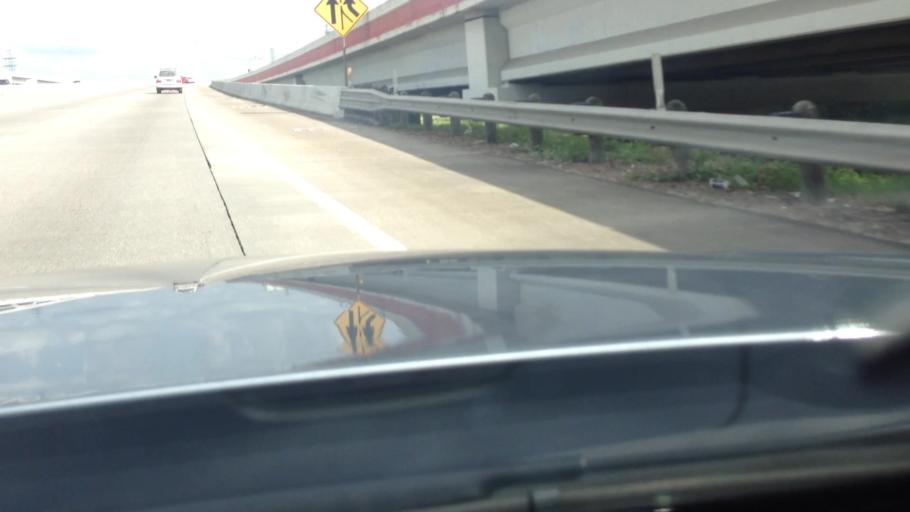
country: US
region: Texas
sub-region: Harris County
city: Hudson
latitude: 29.9425
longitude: -95.5233
